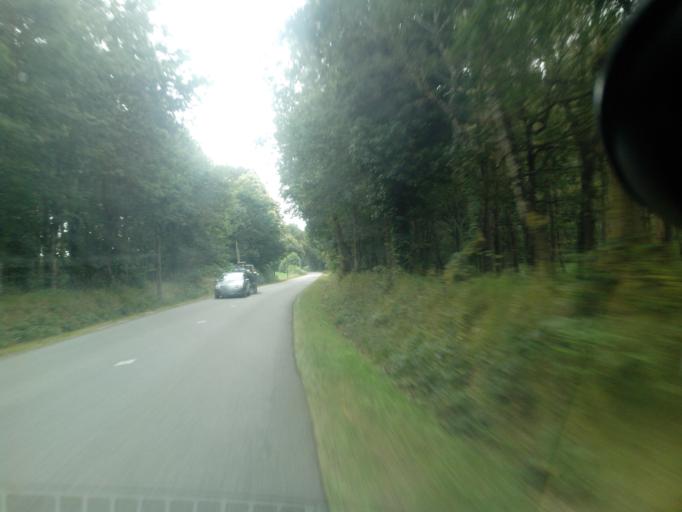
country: FR
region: Brittany
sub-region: Departement du Morbihan
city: Merlevenez
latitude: 47.7125
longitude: -3.2567
